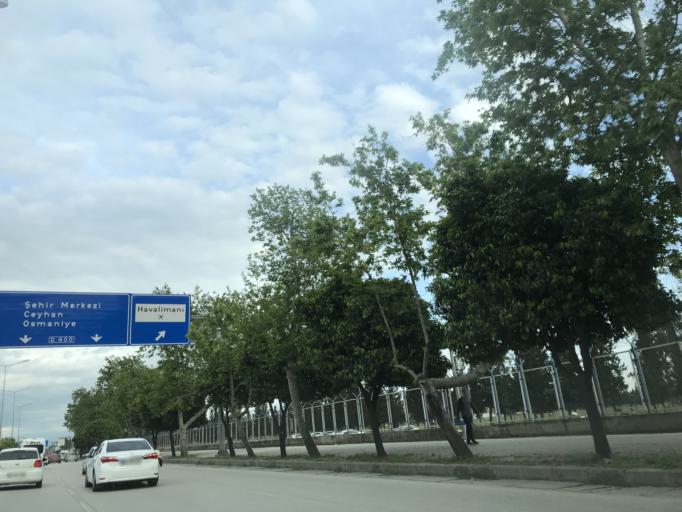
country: TR
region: Adana
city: Seyhan
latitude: 36.9938
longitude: 35.2930
